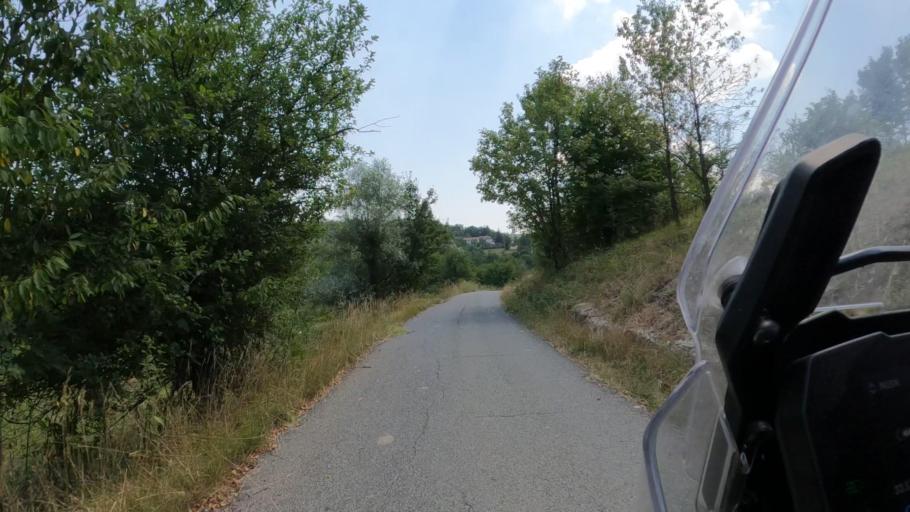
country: IT
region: Piedmont
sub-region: Provincia di Alessandria
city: Cassinelle-Concentrico
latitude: 44.5737
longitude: 8.5553
